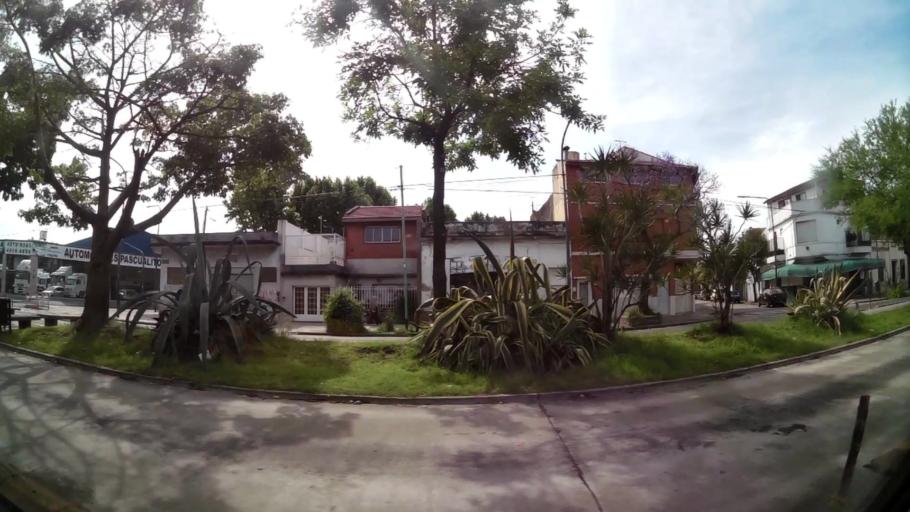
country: AR
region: Buenos Aires F.D.
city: Villa Lugano
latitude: -34.6460
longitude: -58.4265
